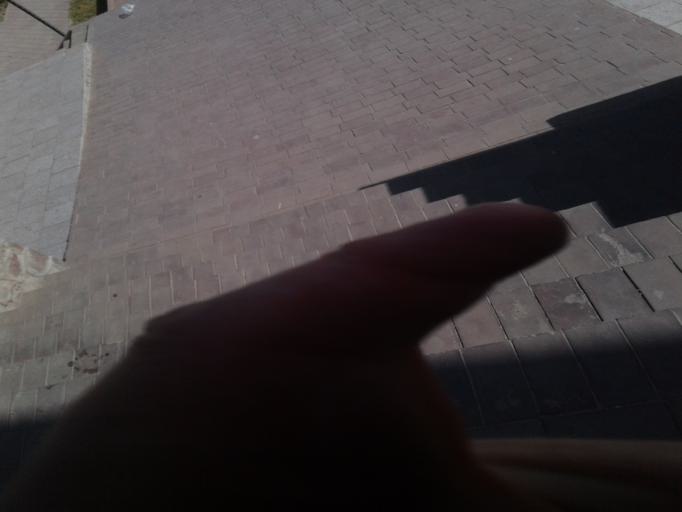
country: TJ
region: Republican Subordination
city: Hisor
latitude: 38.4837
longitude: 68.5937
